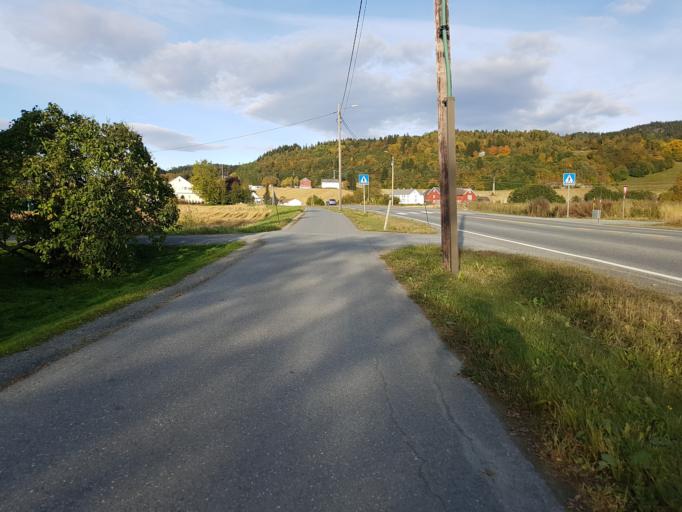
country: NO
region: Sor-Trondelag
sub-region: Trondheim
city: Trondheim
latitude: 63.3772
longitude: 10.4320
